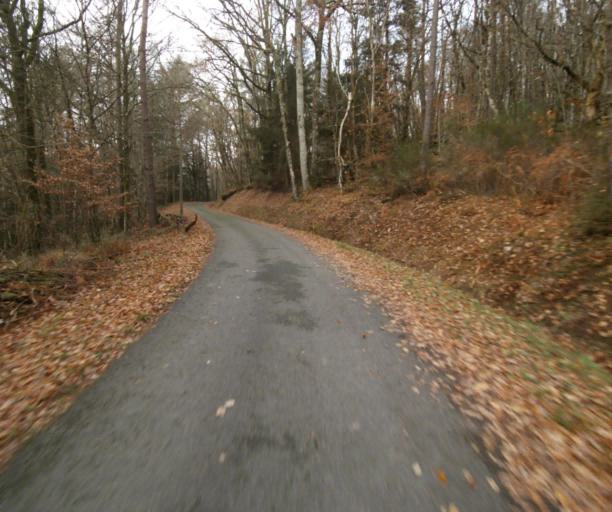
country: FR
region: Limousin
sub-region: Departement de la Correze
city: Chameyrat
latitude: 45.2244
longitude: 1.6979
